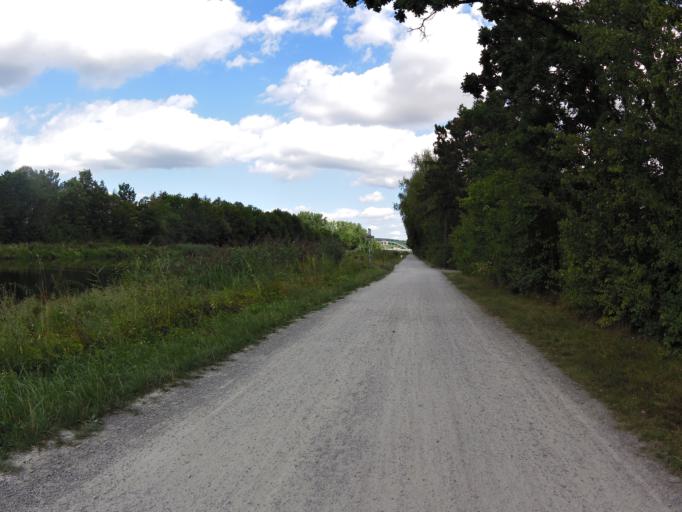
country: DE
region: Bavaria
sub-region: Regierungsbezirk Unterfranken
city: Volkach
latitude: 49.8540
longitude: 10.2257
